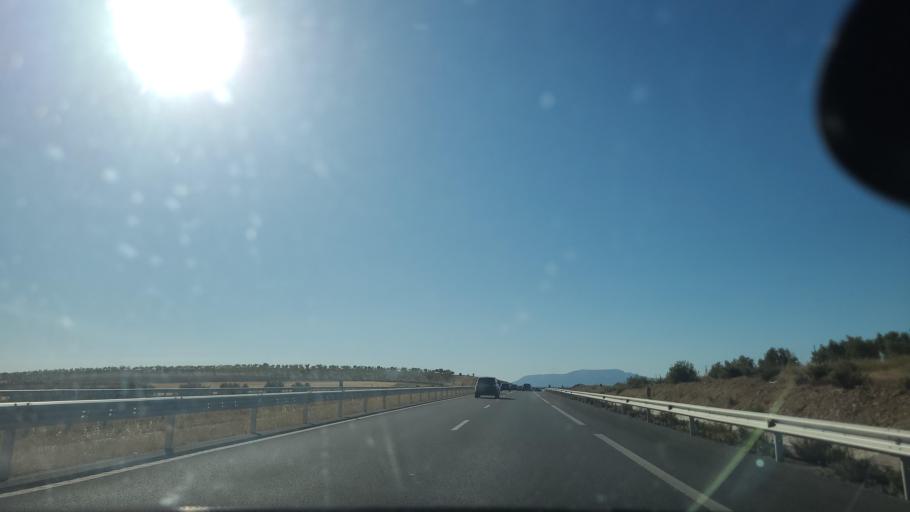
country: ES
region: Andalusia
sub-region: Provincia de Granada
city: Las Gabias
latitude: 37.1370
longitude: -3.6987
